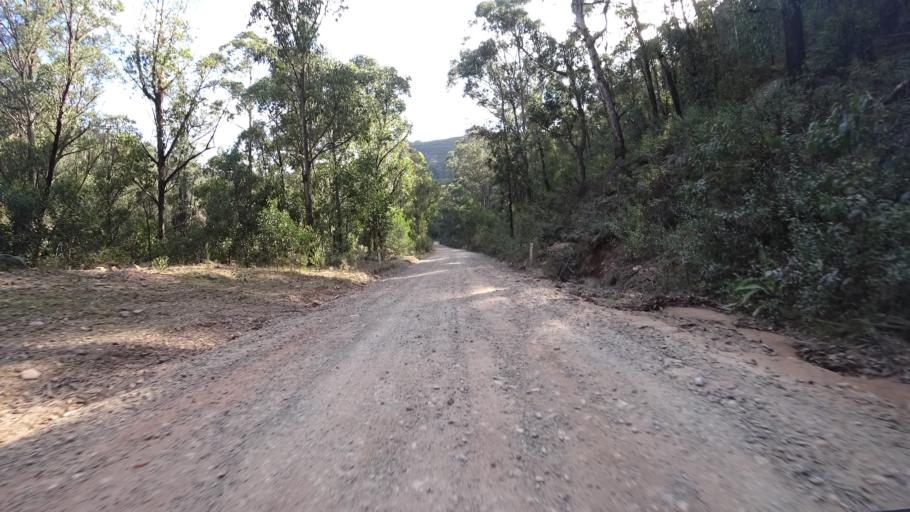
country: AU
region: New South Wales
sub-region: Lithgow
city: Lithgow
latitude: -33.4470
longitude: 150.1783
